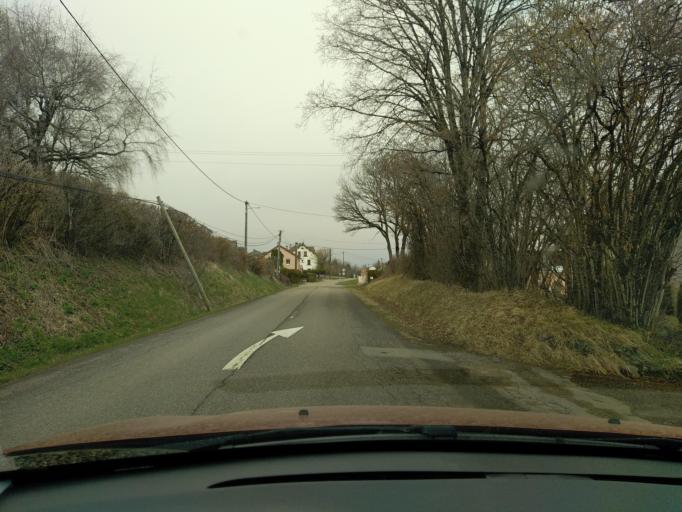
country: FR
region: Franche-Comte
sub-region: Departement du Jura
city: Champagnole
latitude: 46.7781
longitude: 5.8947
